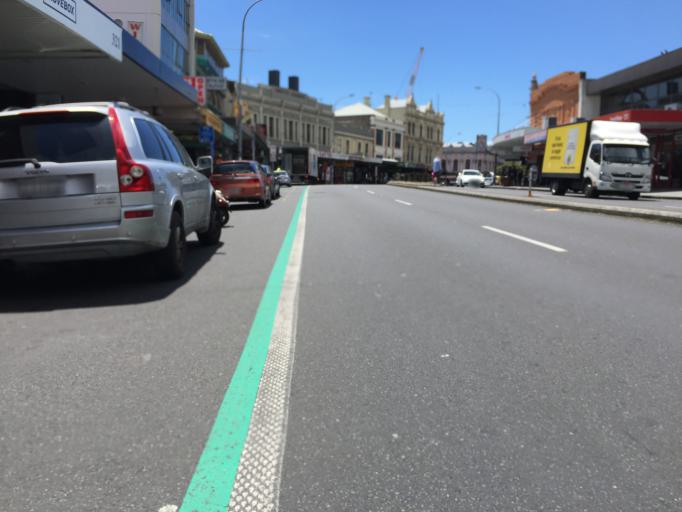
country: NZ
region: Auckland
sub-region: Auckland
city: Auckland
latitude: -36.8578
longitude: 174.7575
